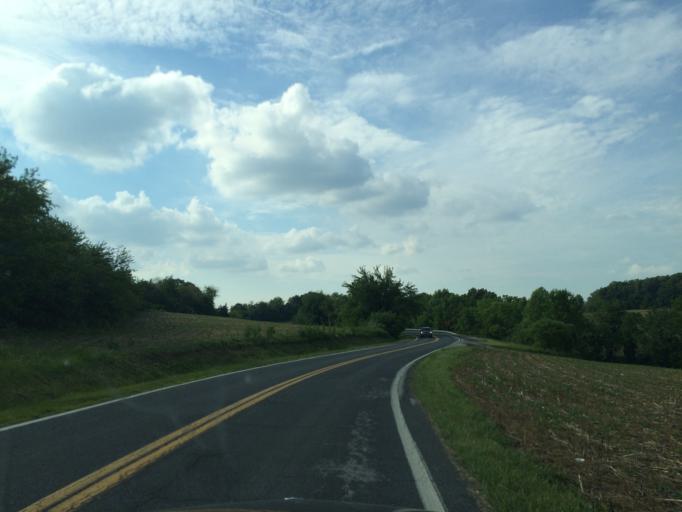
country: US
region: Maryland
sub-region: Carroll County
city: Westminster
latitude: 39.4890
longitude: -76.9948
